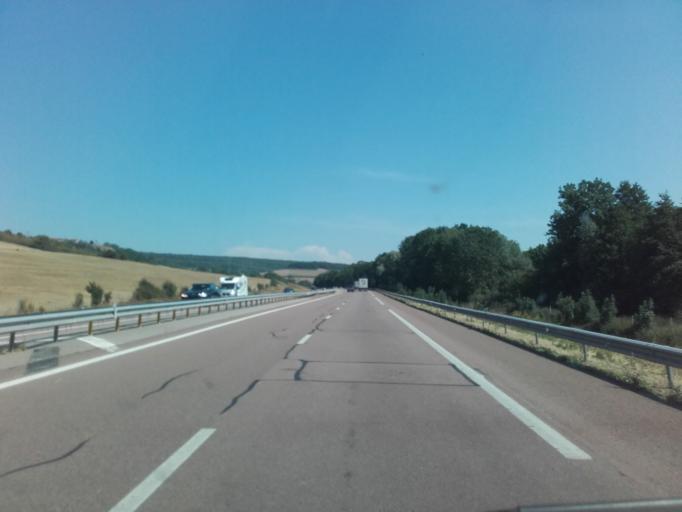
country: FR
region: Bourgogne
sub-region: Departement de la Cote-d'Or
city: Pouilly-en-Auxois
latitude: 47.2016
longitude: 4.6490
